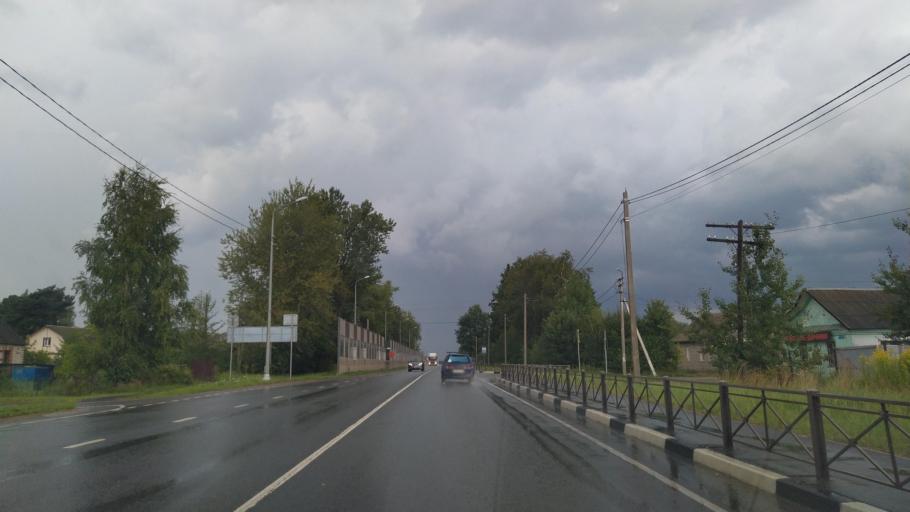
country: RU
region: Pskov
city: Pskov
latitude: 57.7559
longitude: 28.3815
